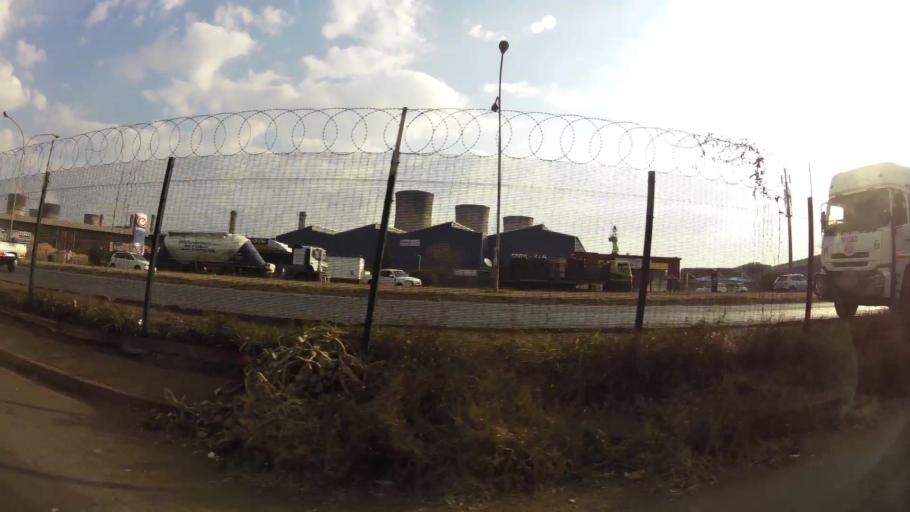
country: ZA
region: Gauteng
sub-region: City of Johannesburg Metropolitan Municipality
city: Modderfontein
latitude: -26.1117
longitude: 28.1980
